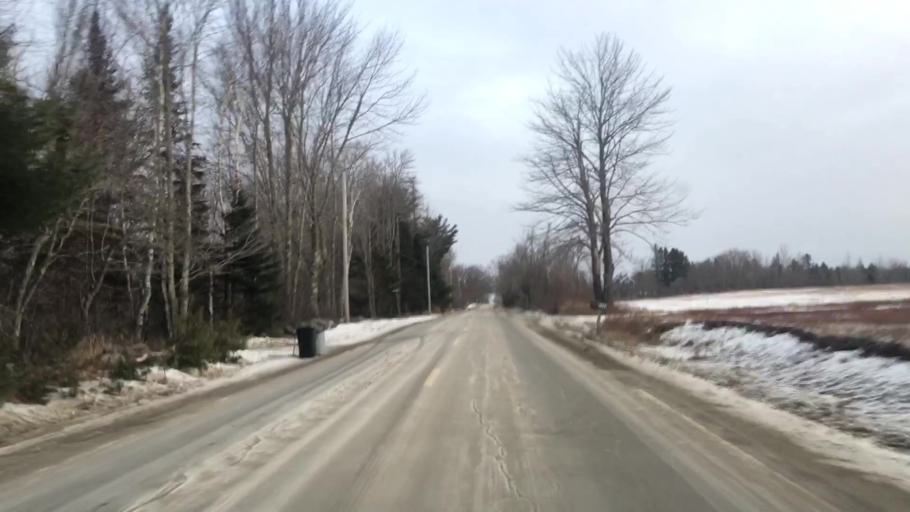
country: US
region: Maine
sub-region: Hancock County
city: Franklin
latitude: 44.7043
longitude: -68.3410
